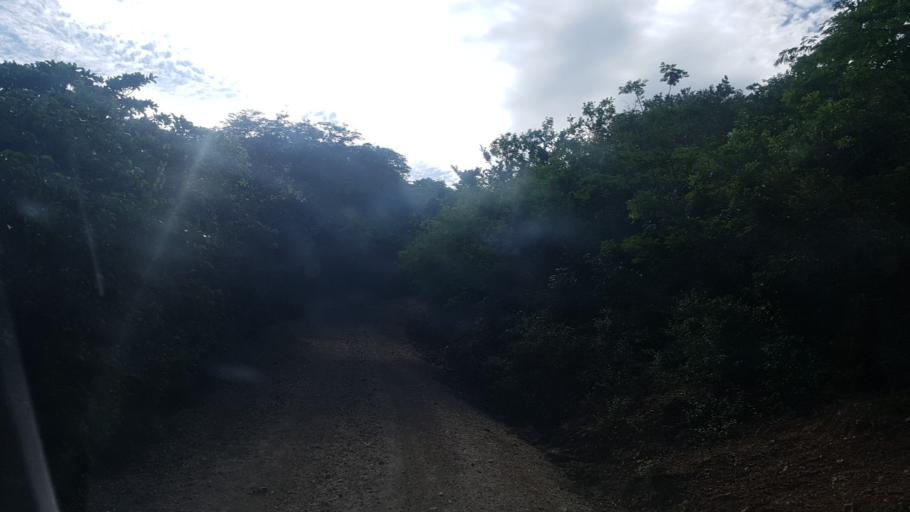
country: NI
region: Nueva Segovia
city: Ocotal
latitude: 13.6076
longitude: -86.4469
